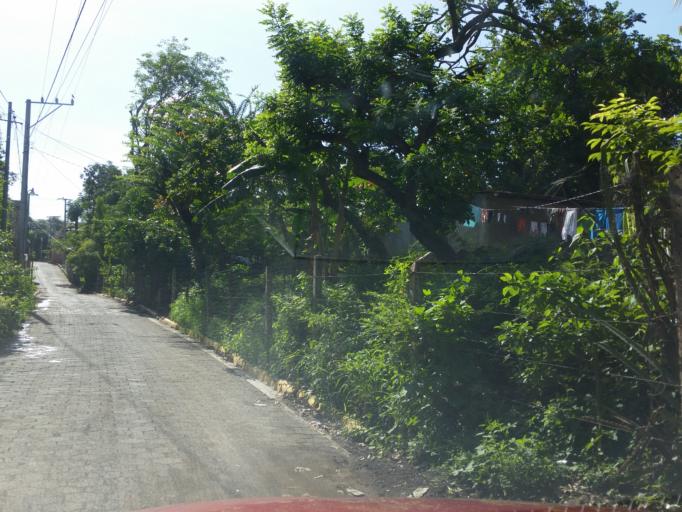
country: NI
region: Managua
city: Managua
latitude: 12.0837
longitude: -86.2373
